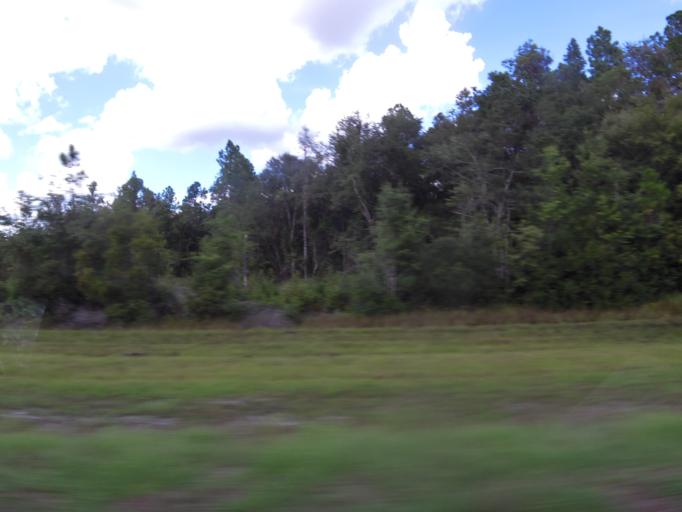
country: US
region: Florida
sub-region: Hamilton County
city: Jasper
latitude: 30.6722
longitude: -82.7642
